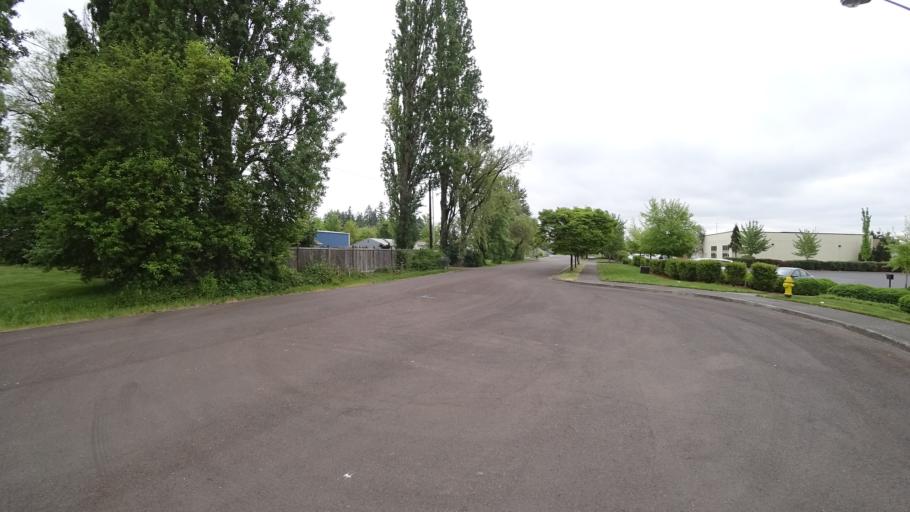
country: US
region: Oregon
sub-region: Washington County
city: Rockcreek
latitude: 45.5670
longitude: -122.8986
